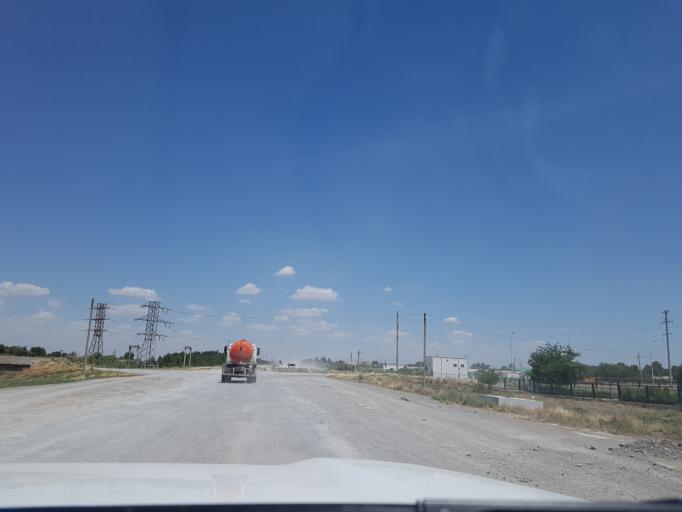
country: TM
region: Ahal
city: Abadan
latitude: 38.1735
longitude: 57.9472
